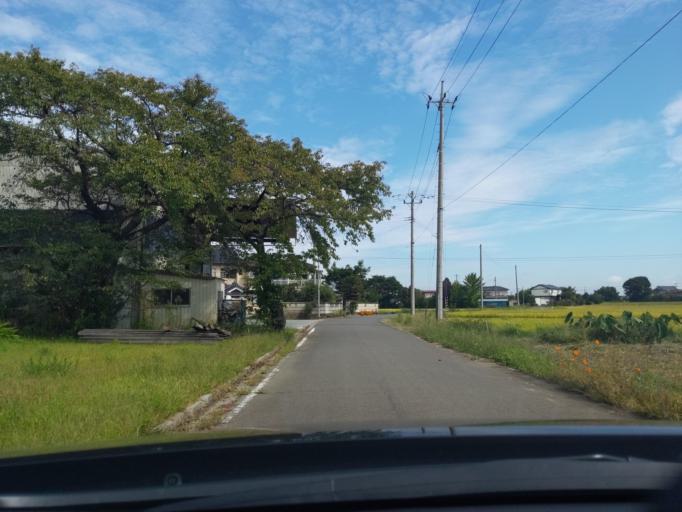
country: JP
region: Fukushima
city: Koriyama
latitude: 37.4352
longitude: 140.3312
